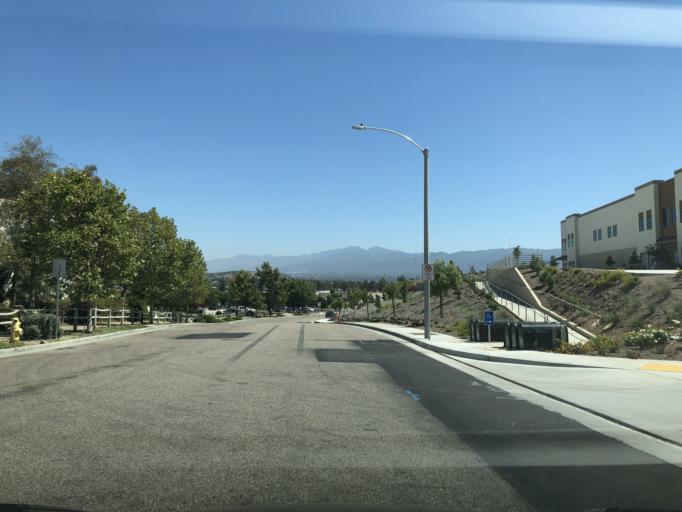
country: US
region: California
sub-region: Riverside County
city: Norco
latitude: 33.9300
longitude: -117.5626
